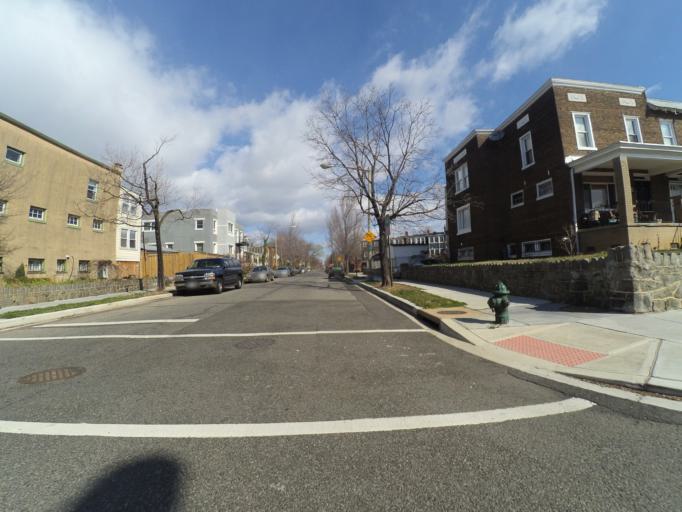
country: US
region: Maryland
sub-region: Prince George's County
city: Silver Hill
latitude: 38.8841
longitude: -76.9790
